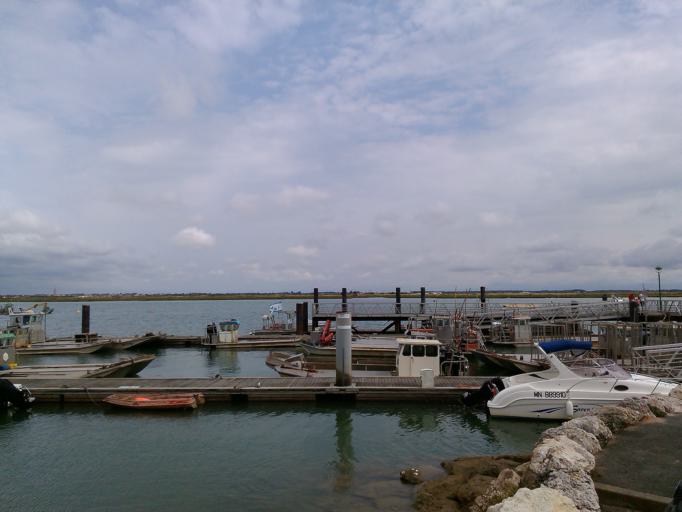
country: FR
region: Poitou-Charentes
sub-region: Departement de la Charente-Maritime
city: La Tremblade
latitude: 45.7815
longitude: -1.1227
